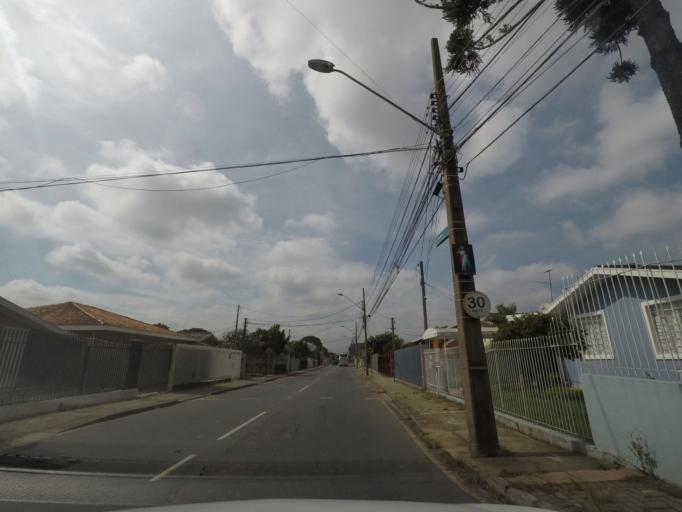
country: BR
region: Parana
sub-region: Curitiba
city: Curitiba
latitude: -25.4795
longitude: -49.3070
